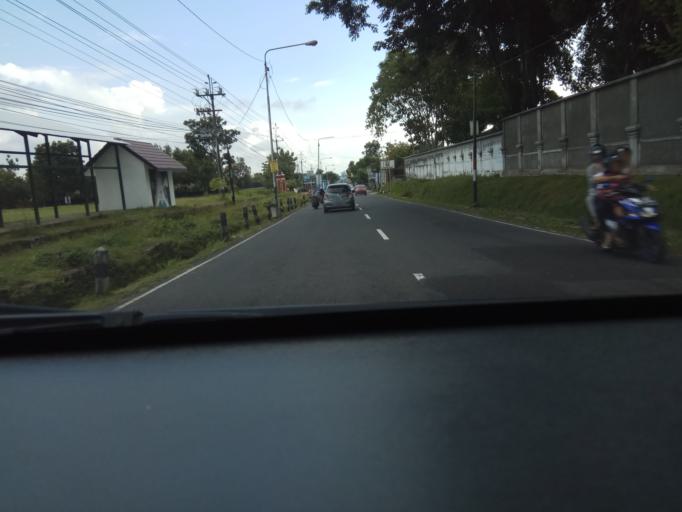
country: ID
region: Daerah Istimewa Yogyakarta
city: Melati
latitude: -7.7151
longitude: 110.4065
